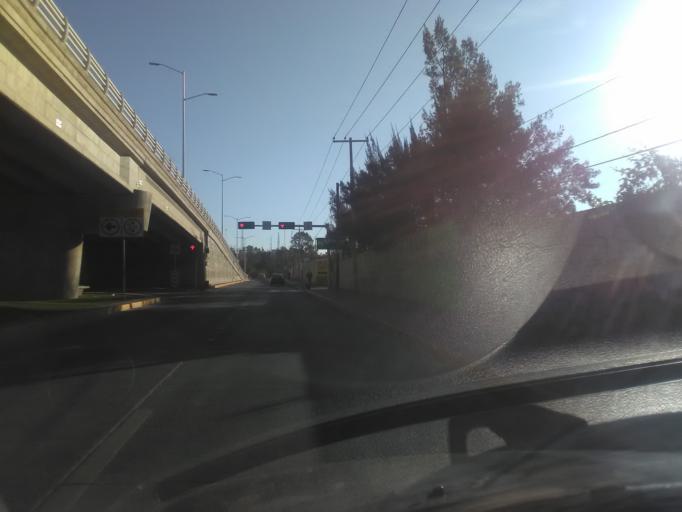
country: MX
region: Durango
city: Victoria de Durango
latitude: 24.0107
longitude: -104.6917
